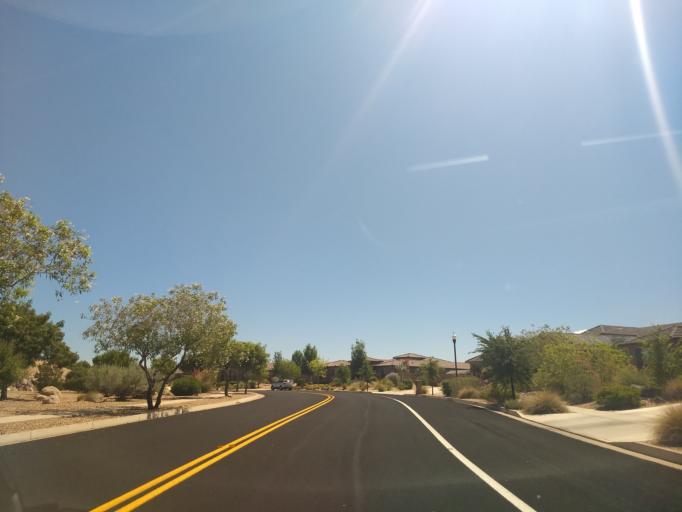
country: US
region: Utah
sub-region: Washington County
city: Washington
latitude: 37.1432
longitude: -113.4647
